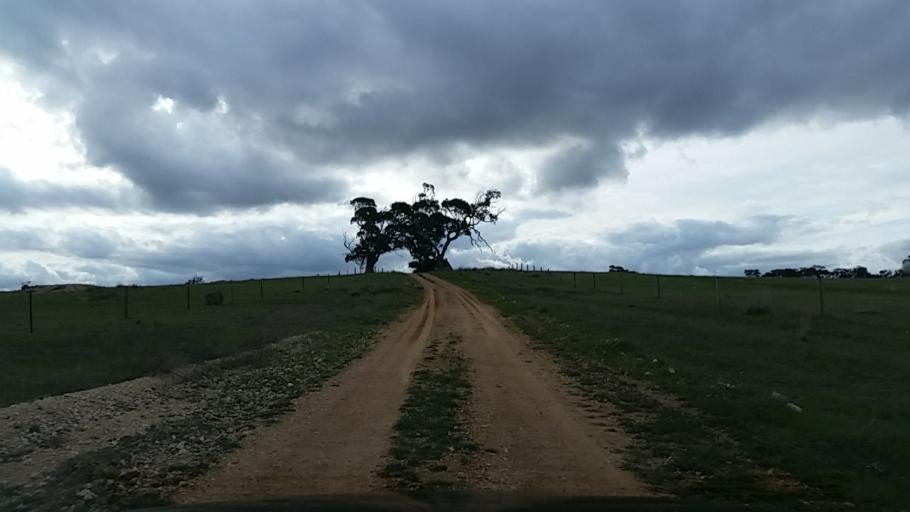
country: AU
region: South Australia
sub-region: Mount Barker
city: Callington
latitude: -34.9640
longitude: 139.0541
